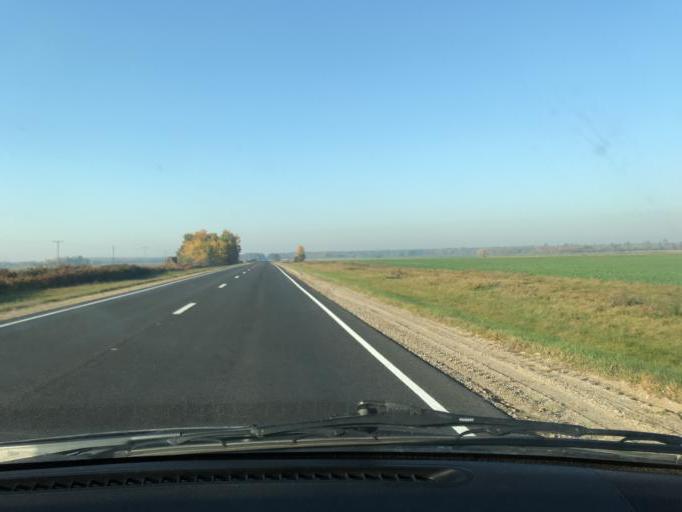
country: BY
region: Brest
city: Baranovichi
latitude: 52.8944
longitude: 25.8410
